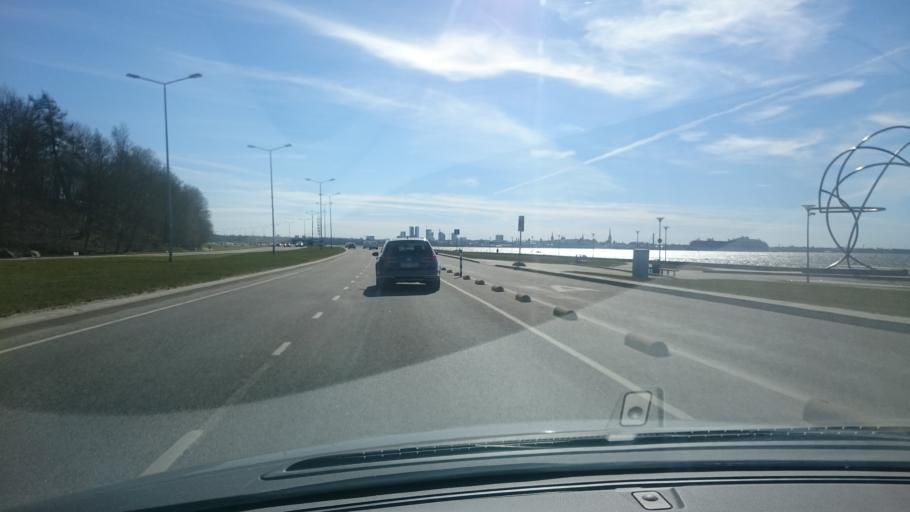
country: EE
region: Harju
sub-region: Viimsi vald
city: Viimsi
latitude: 59.4593
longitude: 24.8143
